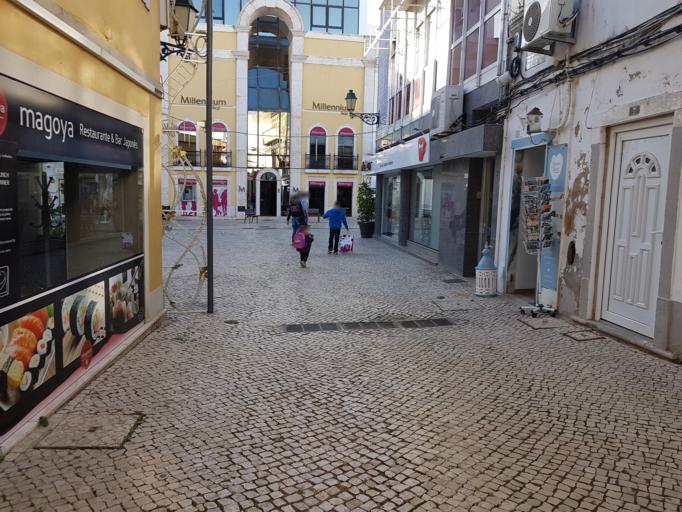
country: PT
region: Faro
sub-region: Faro
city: Faro
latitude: 37.0158
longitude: -7.9331
